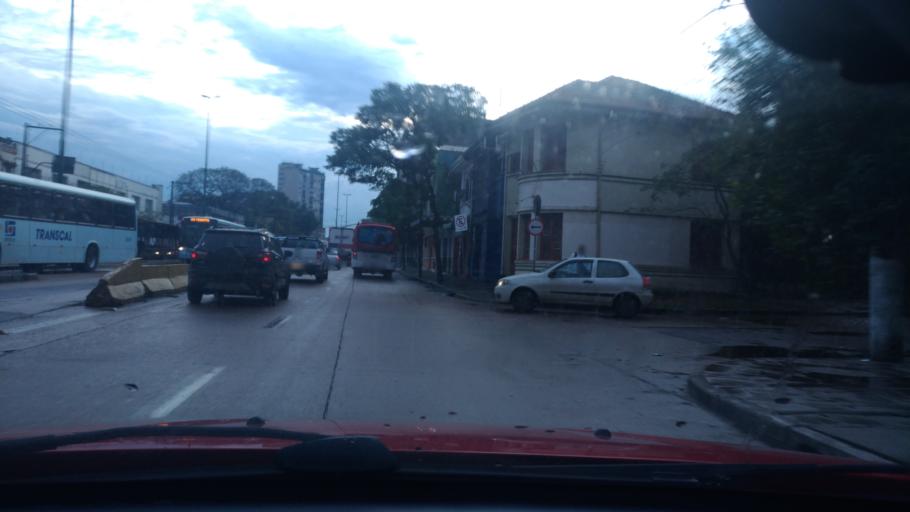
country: BR
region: Rio Grande do Sul
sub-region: Porto Alegre
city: Porto Alegre
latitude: -30.0169
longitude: -51.2078
